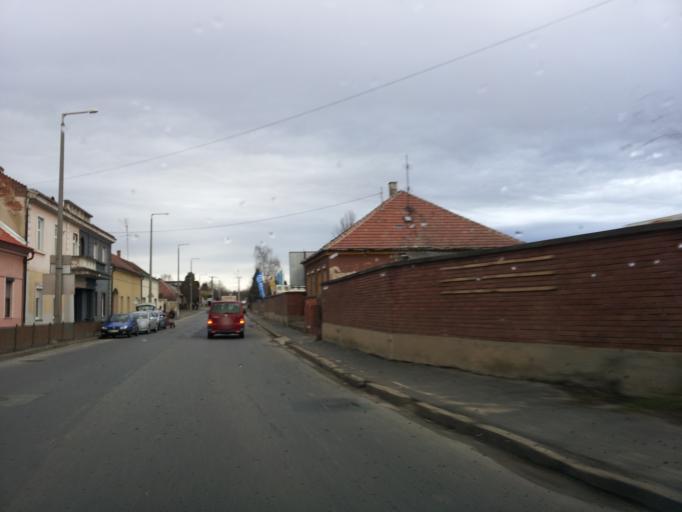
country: HU
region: Vas
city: Koszeg
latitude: 47.3816
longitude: 16.5555
